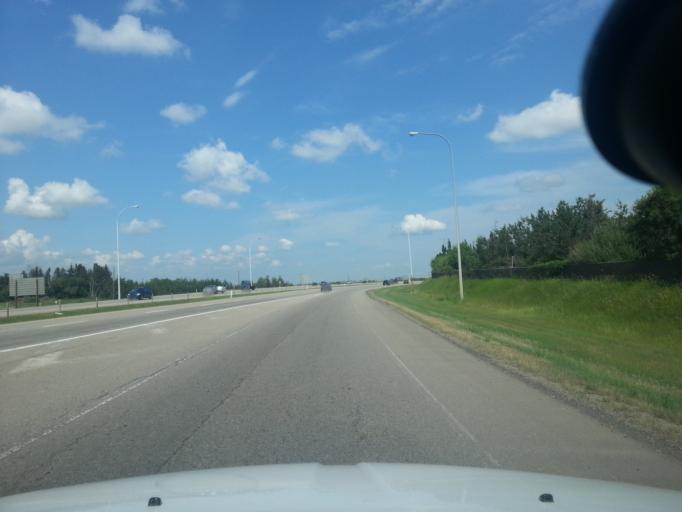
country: CA
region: Alberta
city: Leduc
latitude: 53.2699
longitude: -113.5613
